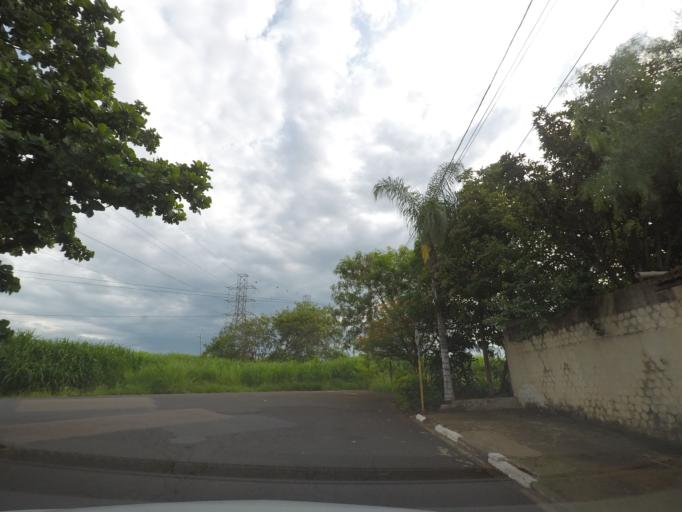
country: BR
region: Sao Paulo
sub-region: Campinas
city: Campinas
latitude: -22.8874
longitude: -47.1297
